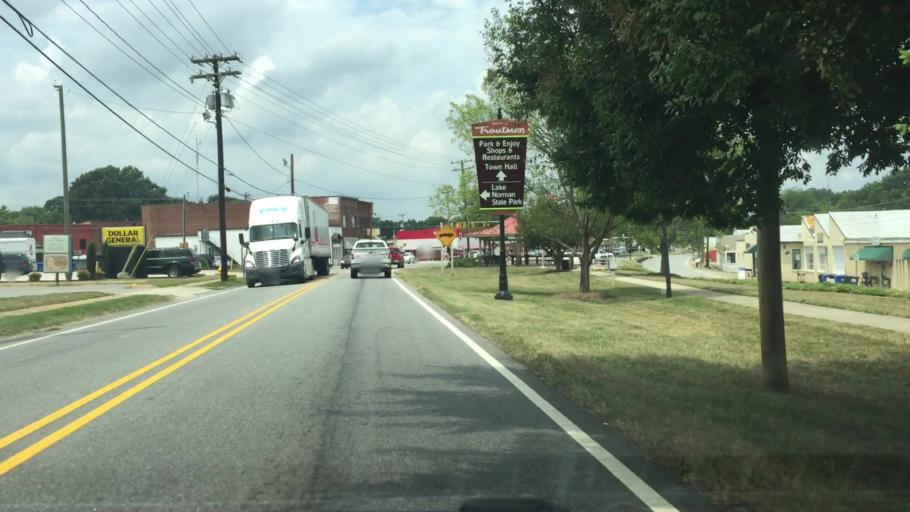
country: US
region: North Carolina
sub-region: Iredell County
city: Troutman
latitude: 35.7011
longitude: -80.8872
